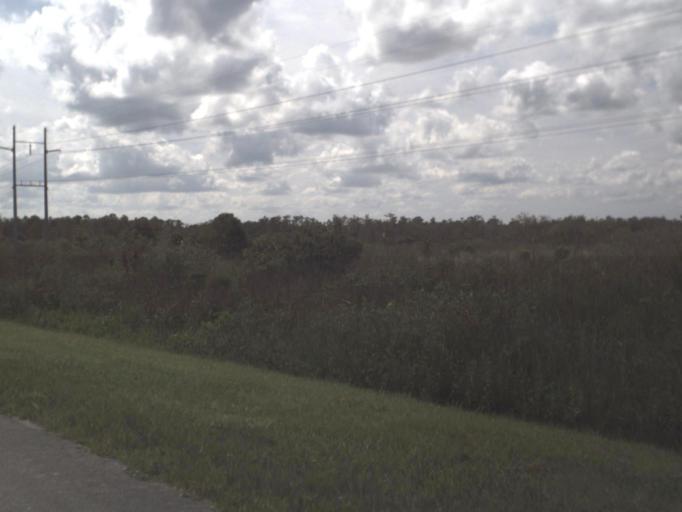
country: US
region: Florida
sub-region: Collier County
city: Orangetree
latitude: 26.1201
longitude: -81.3449
